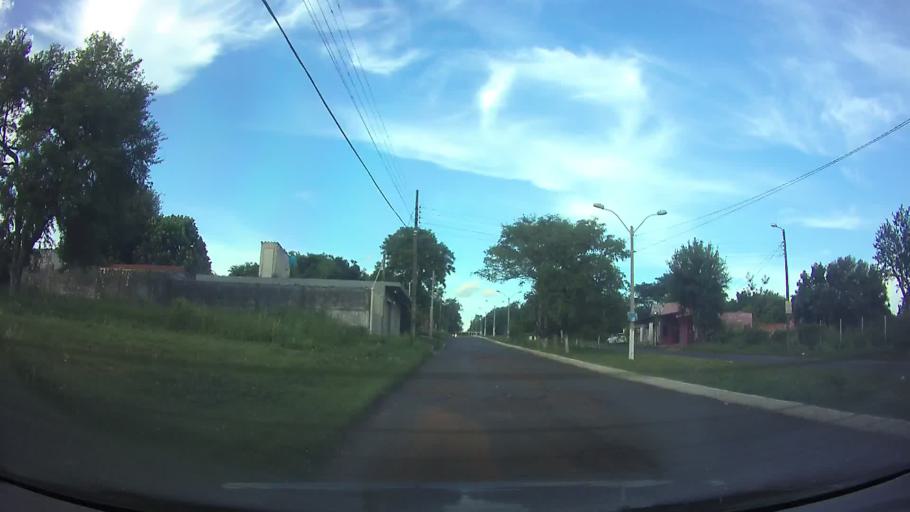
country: PY
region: Central
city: San Antonio
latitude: -25.4301
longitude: -57.5485
